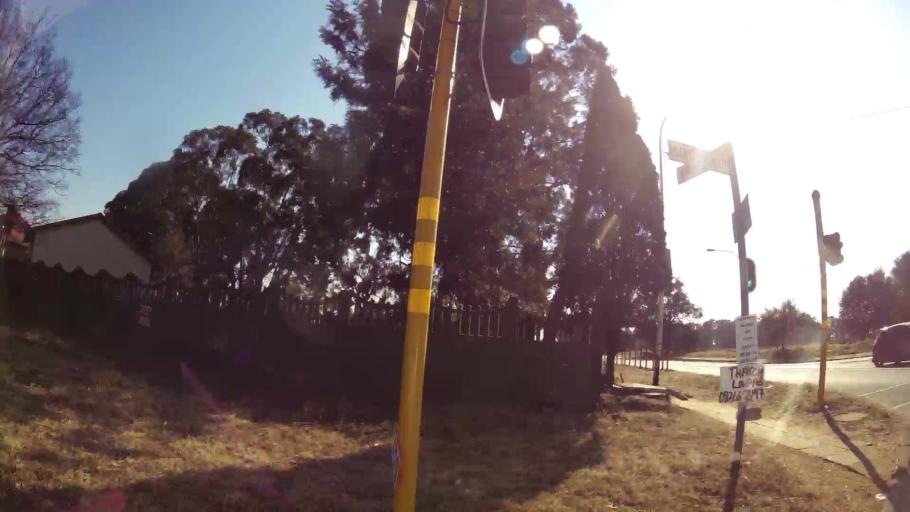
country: ZA
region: Gauteng
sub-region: Ekurhuleni Metropolitan Municipality
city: Boksburg
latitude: -26.2205
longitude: 28.2635
